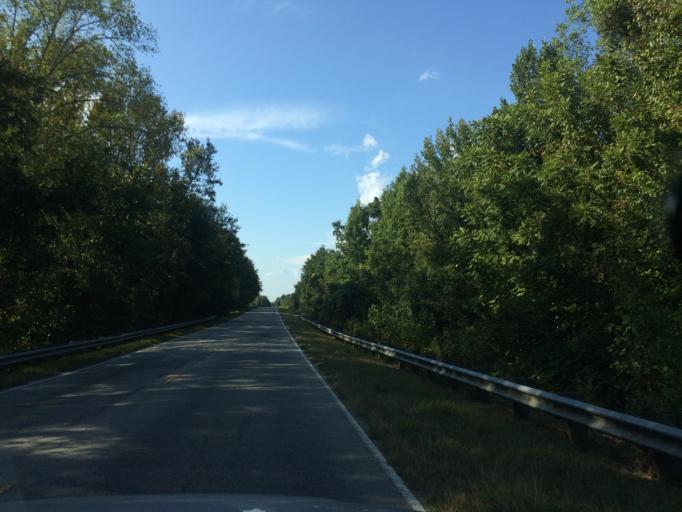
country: US
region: South Carolina
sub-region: Laurens County
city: Laurens
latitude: 34.5556
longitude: -82.0770
